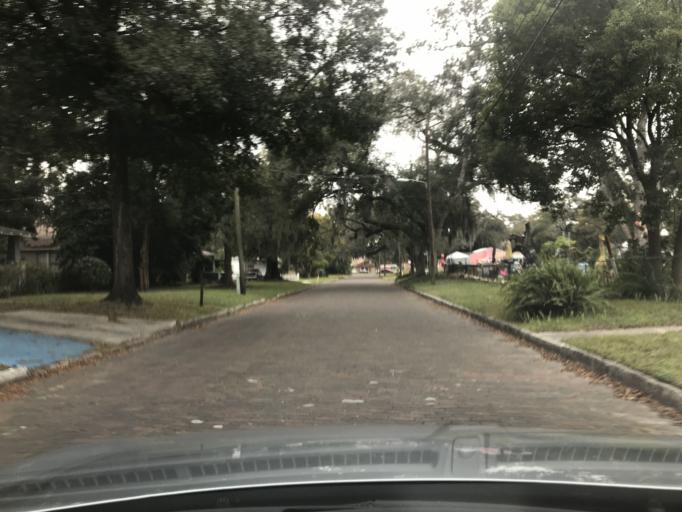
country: US
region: Florida
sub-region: Hillsborough County
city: Tampa
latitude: 27.9834
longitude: -82.4654
